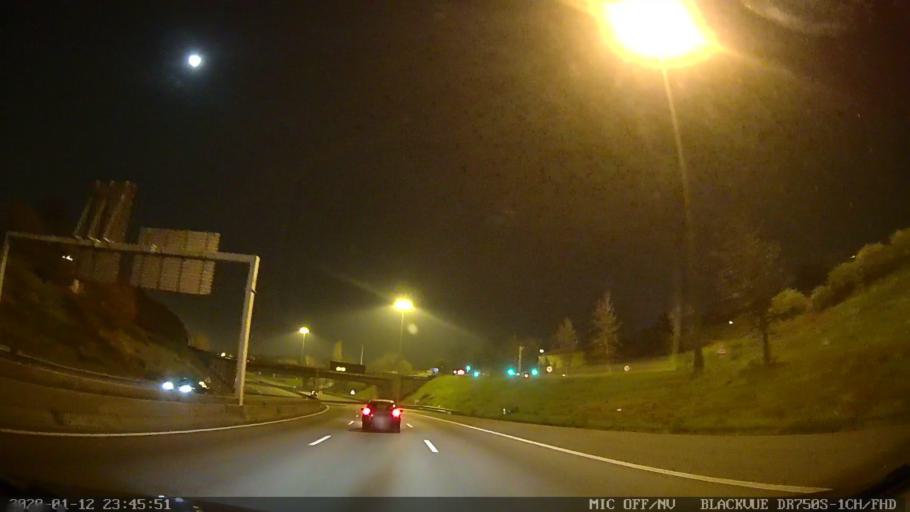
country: PT
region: Porto
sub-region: Porto
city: Porto
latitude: 41.1723
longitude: -8.6071
